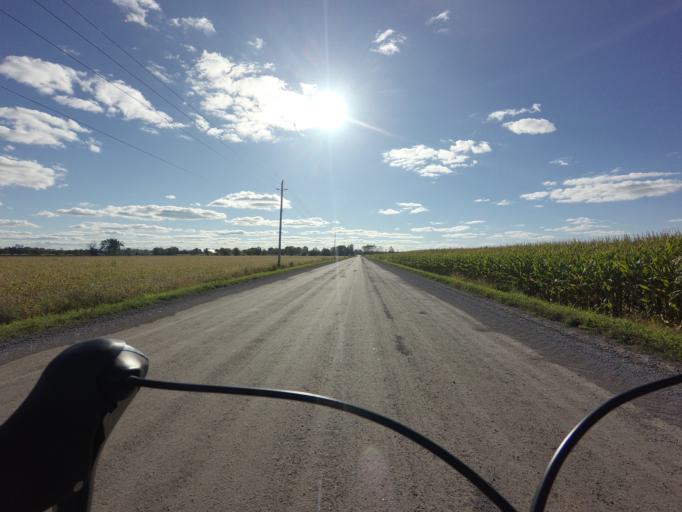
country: CA
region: Ontario
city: Bells Corners
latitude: 45.1198
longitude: -75.6923
